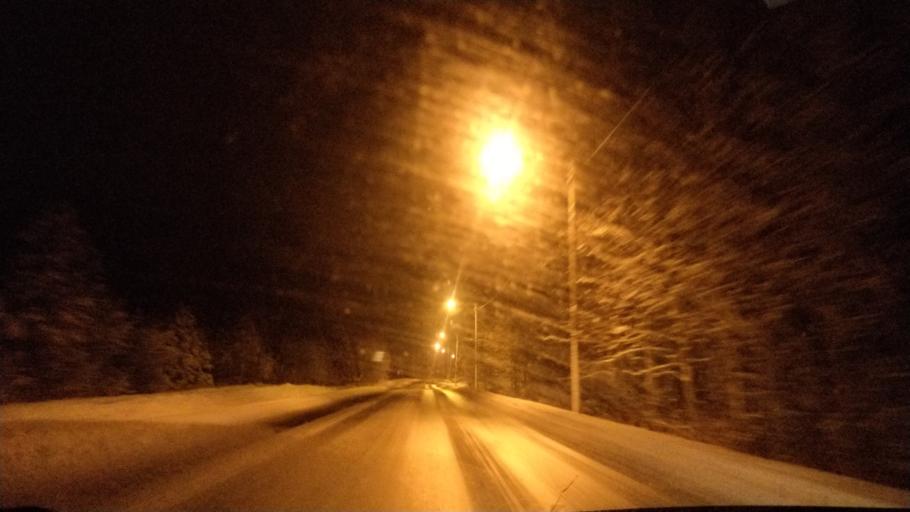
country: FI
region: Lapland
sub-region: Rovaniemi
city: Rovaniemi
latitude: 66.4010
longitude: 25.3887
